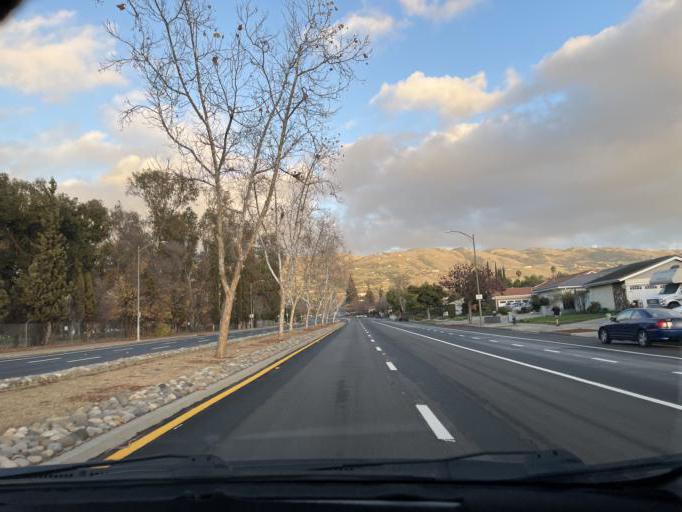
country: US
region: California
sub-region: Santa Clara County
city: Alum Rock
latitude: 37.3363
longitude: -121.7965
